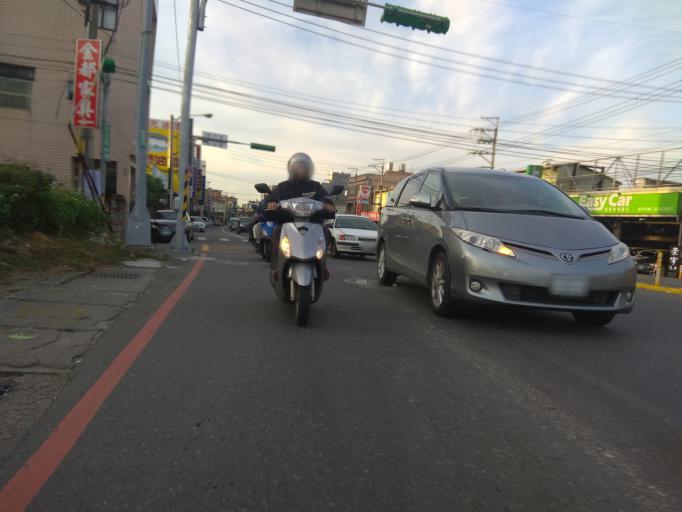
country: TW
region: Taiwan
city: Taoyuan City
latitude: 24.9659
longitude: 121.2040
